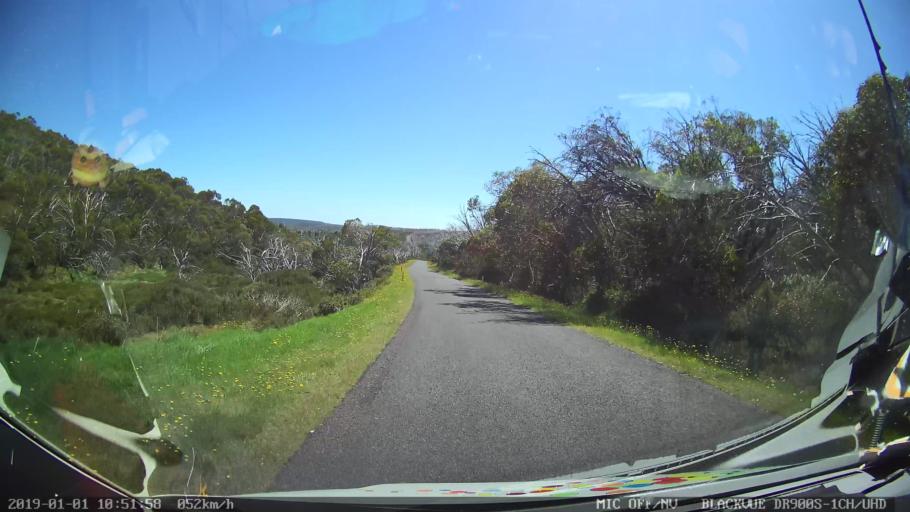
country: AU
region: New South Wales
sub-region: Snowy River
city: Jindabyne
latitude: -36.0188
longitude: 148.3765
